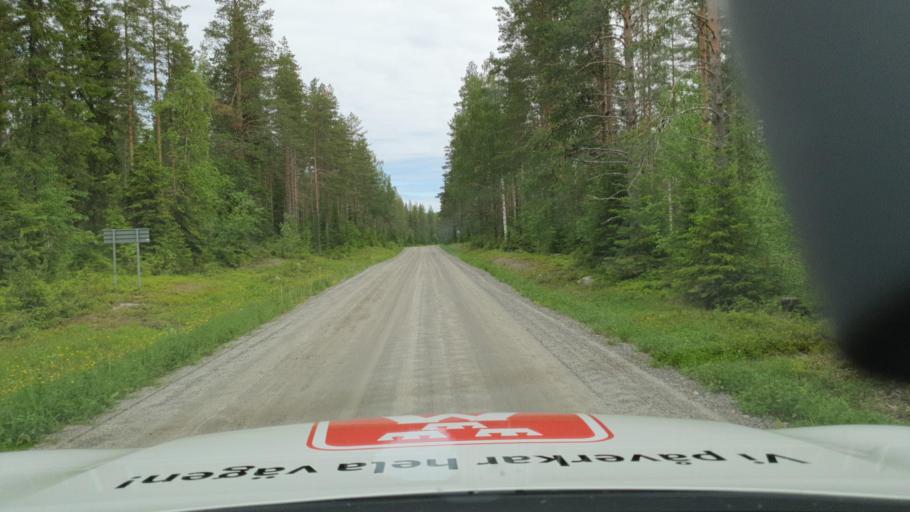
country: SE
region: Vaesterbotten
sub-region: Skelleftea Kommun
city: Langsele
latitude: 64.4851
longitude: 20.2522
